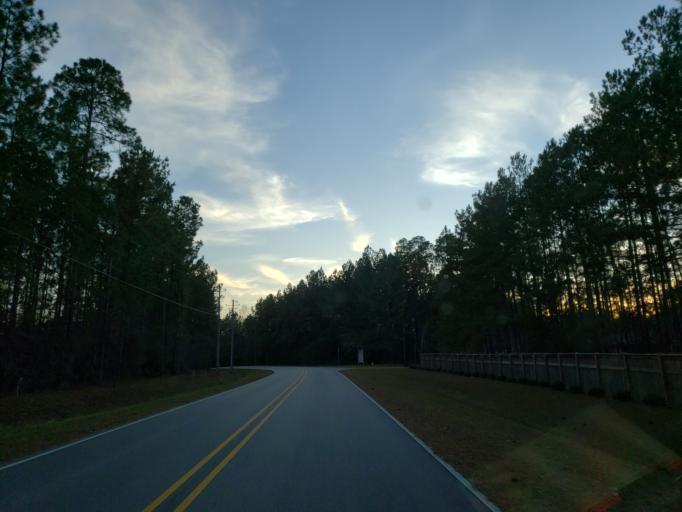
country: US
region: Mississippi
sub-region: Forrest County
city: Hattiesburg
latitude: 31.2734
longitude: -89.3089
